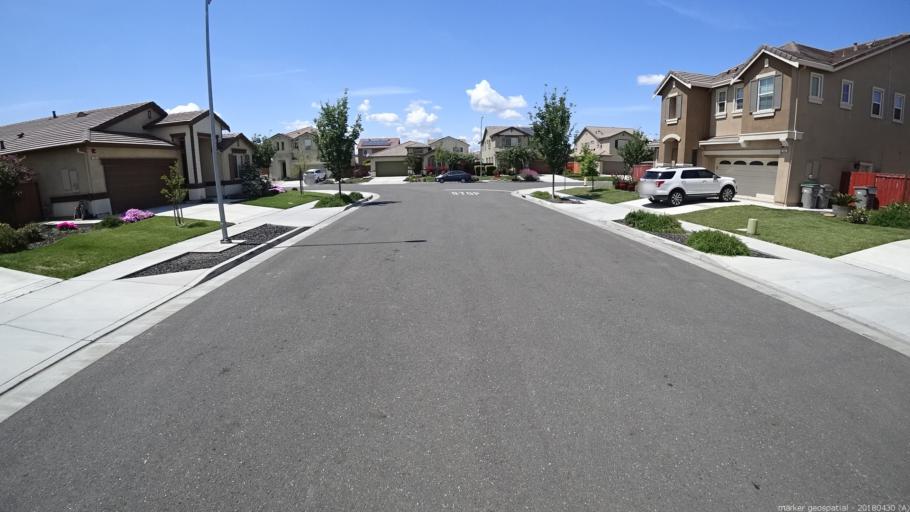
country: US
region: California
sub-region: Yolo County
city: West Sacramento
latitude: 38.5505
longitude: -121.5206
